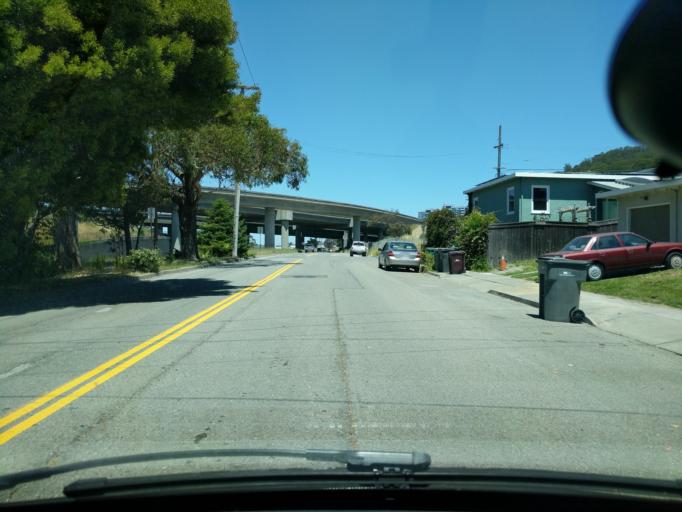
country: US
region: California
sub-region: Alameda County
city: Albany
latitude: 37.8889
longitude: -122.3073
